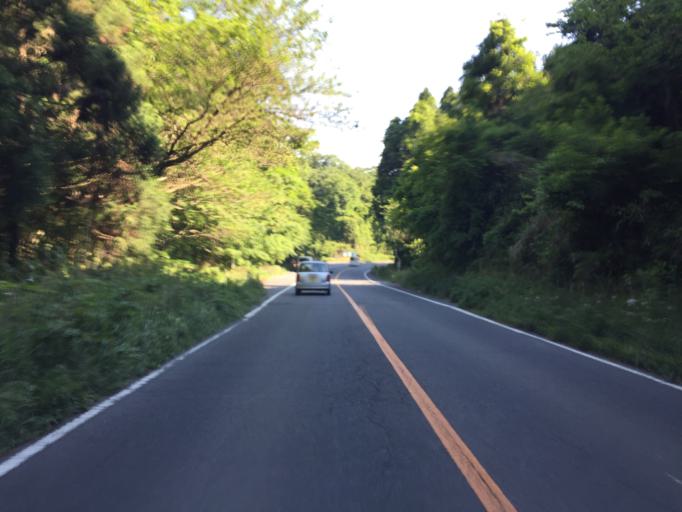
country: JP
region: Fukushima
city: Iwaki
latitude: 36.9470
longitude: 140.8245
